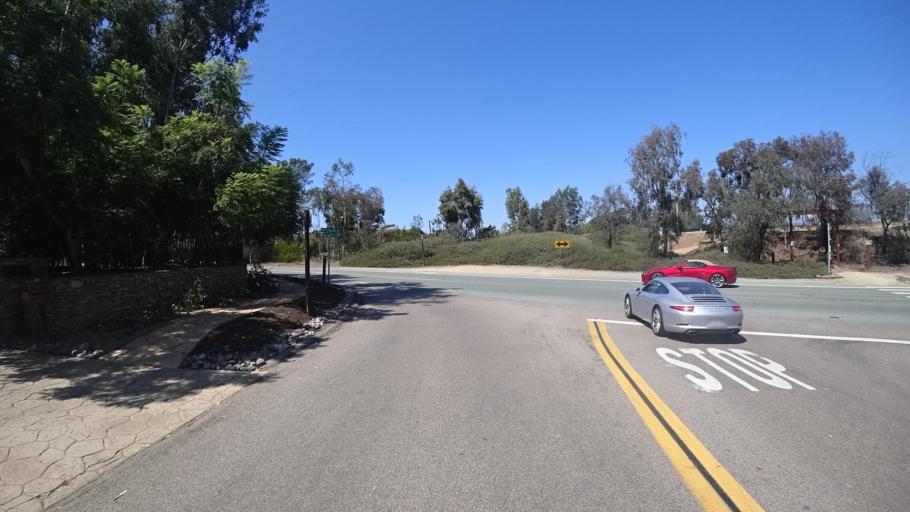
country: US
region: California
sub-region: San Diego County
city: Solana Beach
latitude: 32.9958
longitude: -117.2370
